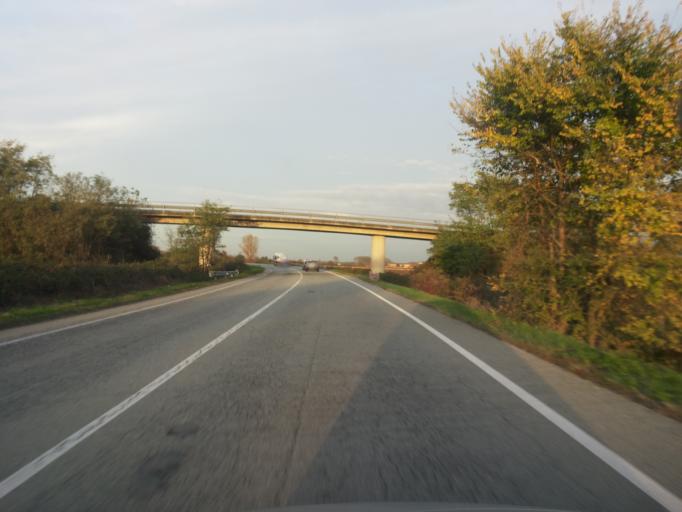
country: IT
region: Piedmont
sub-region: Provincia di Vercelli
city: Tricerro
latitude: 45.2304
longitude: 8.3273
